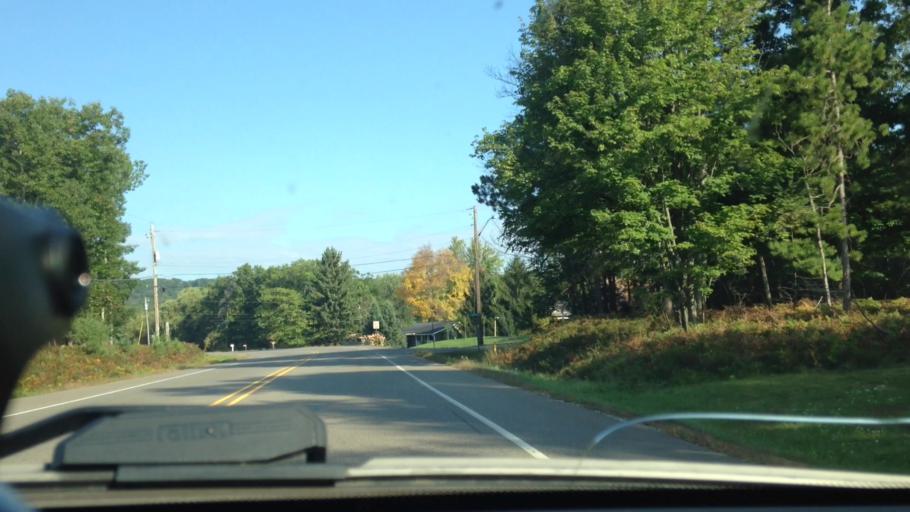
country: US
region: Michigan
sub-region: Dickinson County
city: Quinnesec
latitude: 45.8360
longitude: -88.0093
